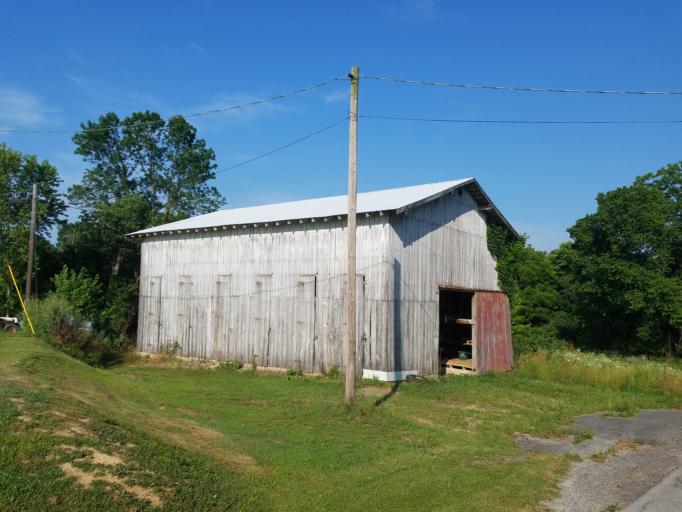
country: US
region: Kentucky
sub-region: Grayson County
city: Leitchfield
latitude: 37.3748
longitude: -86.1086
